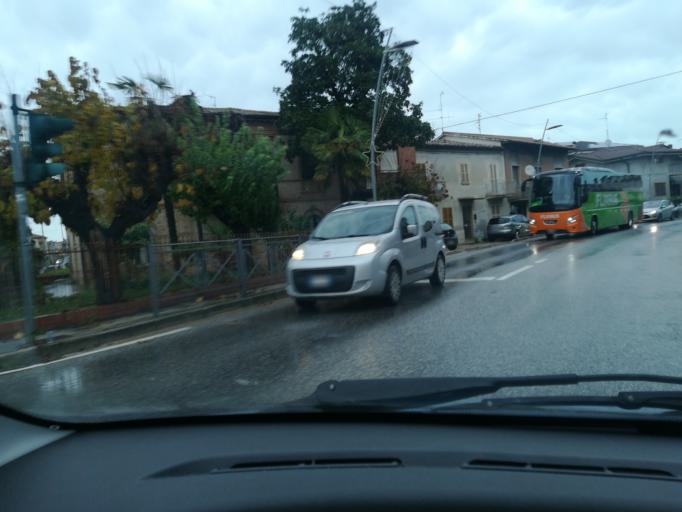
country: IT
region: The Marches
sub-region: Provincia di Macerata
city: Trodica
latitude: 43.2739
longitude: 13.5929
